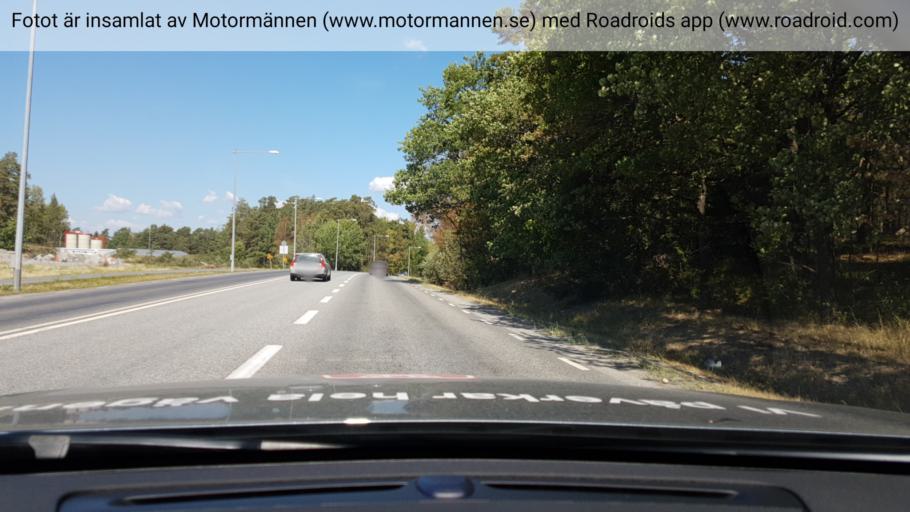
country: SE
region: Stockholm
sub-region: Ekero Kommun
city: Ekeroe
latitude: 59.3113
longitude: 17.8607
